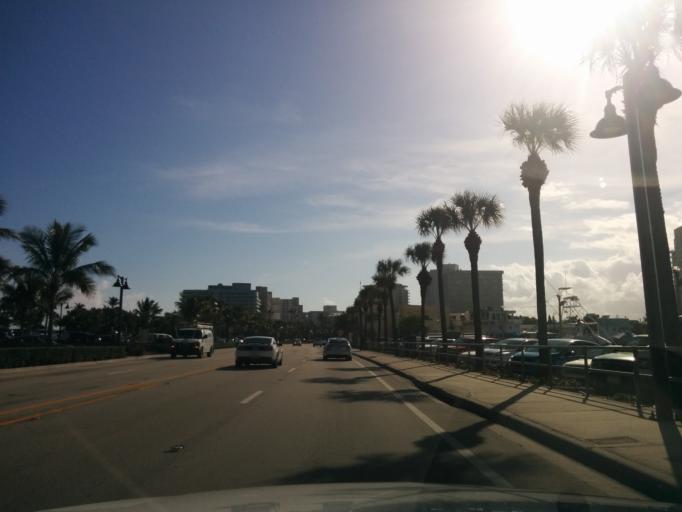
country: US
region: Florida
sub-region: Broward County
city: Sunrise
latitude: 26.1121
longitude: -80.1058
